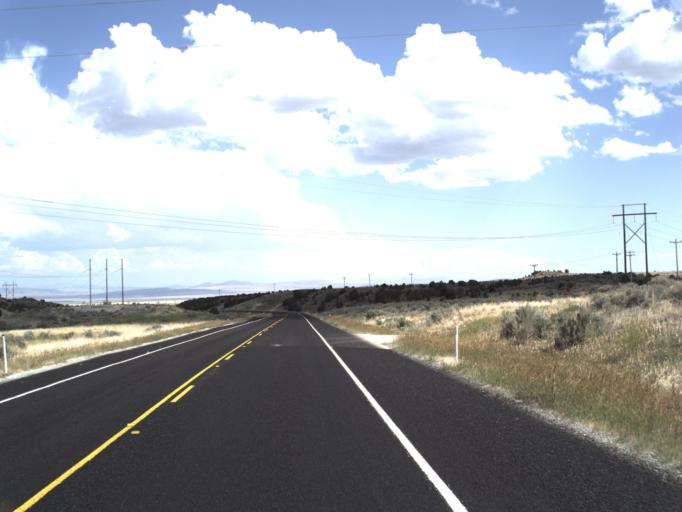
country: US
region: Idaho
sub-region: Minidoka County
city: Rupert
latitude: 41.9777
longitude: -113.1629
